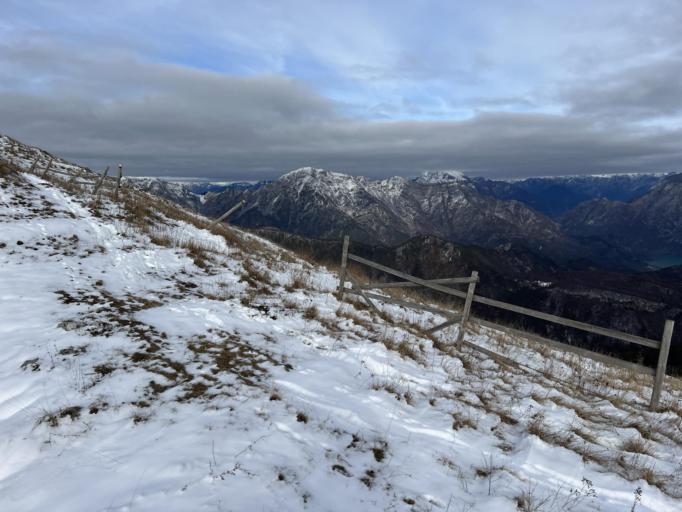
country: IT
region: Friuli Venezia Giulia
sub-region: Provincia di Pordenone
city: Anduins
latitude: 46.2802
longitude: 12.9823
